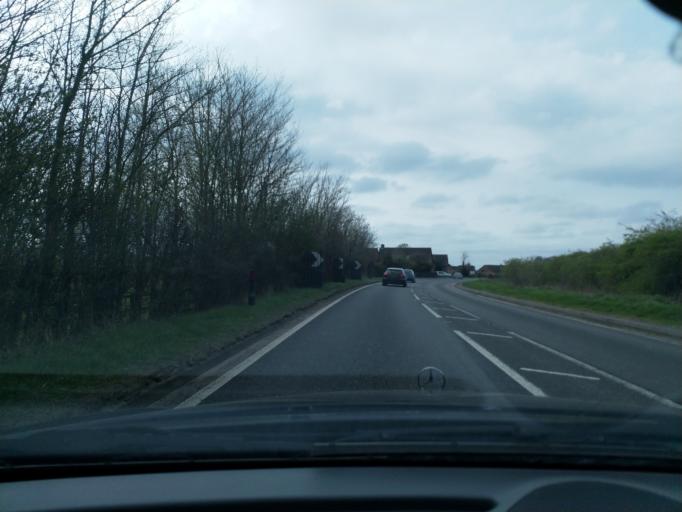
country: GB
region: England
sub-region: Warwickshire
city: Stratford-upon-Avon
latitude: 52.2090
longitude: -1.6813
